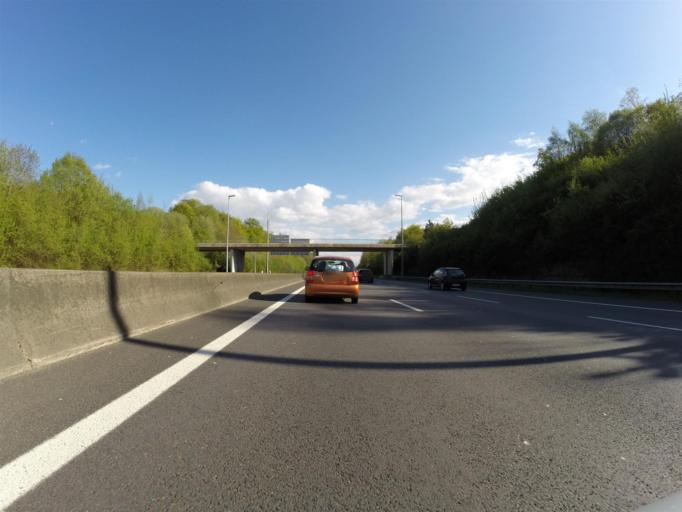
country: LU
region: Luxembourg
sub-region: Canton de Luxembourg
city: Hesperange
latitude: 49.5666
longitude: 6.1279
